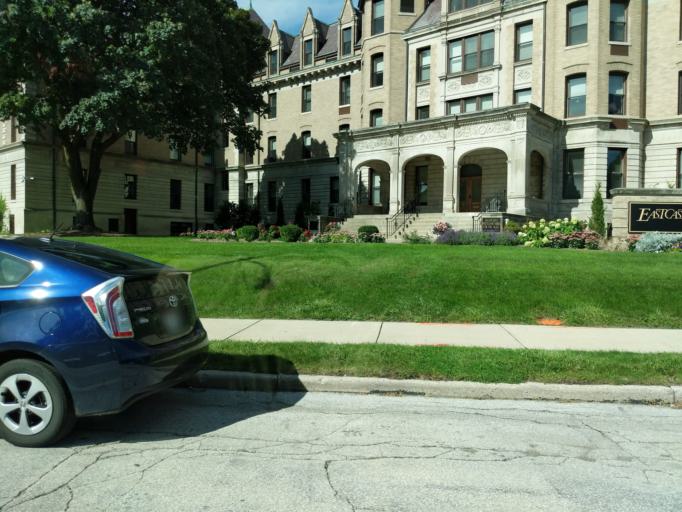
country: US
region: Wisconsin
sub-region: Milwaukee County
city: Shorewood
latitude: 43.0630
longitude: -87.8782
